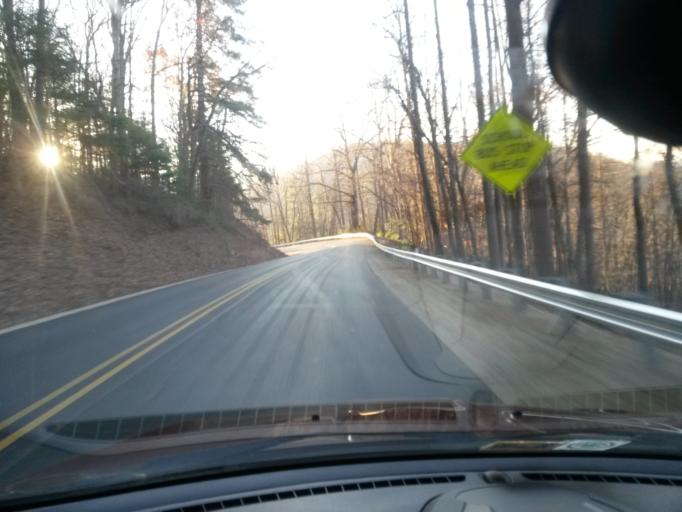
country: US
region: Virginia
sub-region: City of Buena Vista
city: Buena Vista
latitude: 37.7505
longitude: -79.2825
